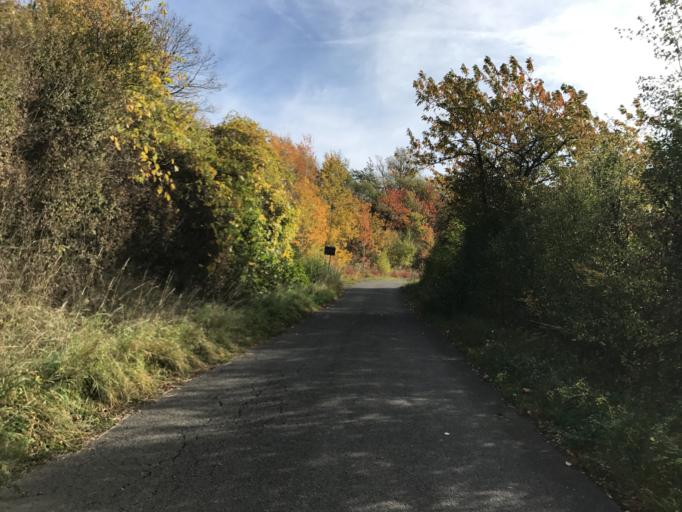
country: DE
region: Rheinland-Pfalz
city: Aspisheim
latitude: 49.9215
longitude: 7.9828
